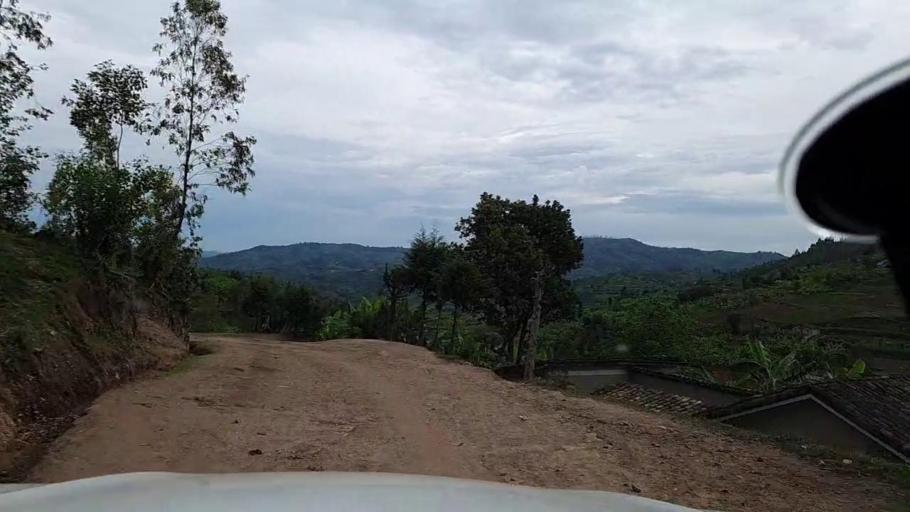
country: RW
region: Southern Province
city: Gitarama
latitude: -2.1289
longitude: 29.6606
